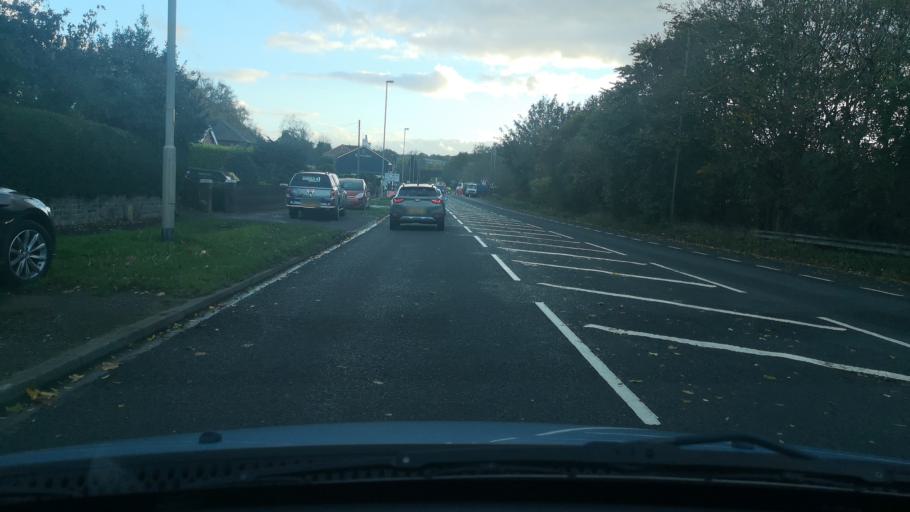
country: GB
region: England
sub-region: City and Borough of Wakefield
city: Crigglestone
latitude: 53.6438
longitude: -1.5464
